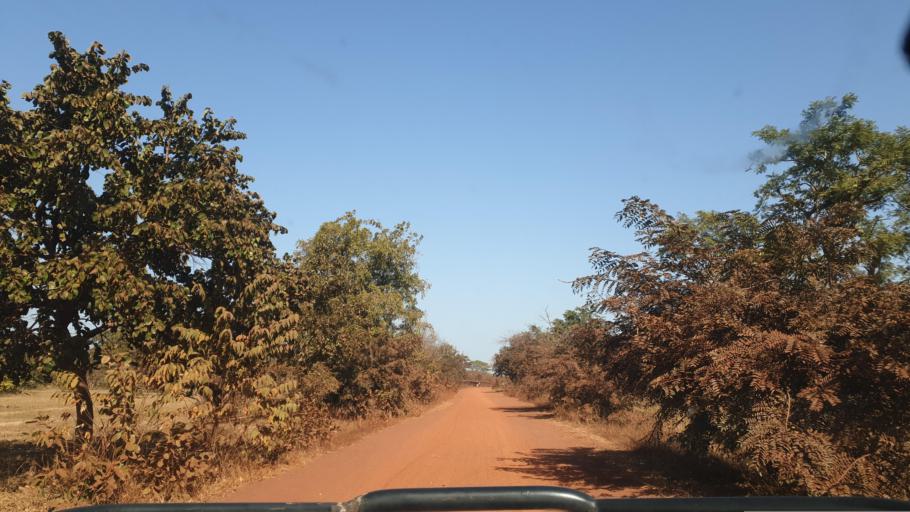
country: ML
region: Sikasso
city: Bougouni
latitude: 11.8451
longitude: -6.9784
